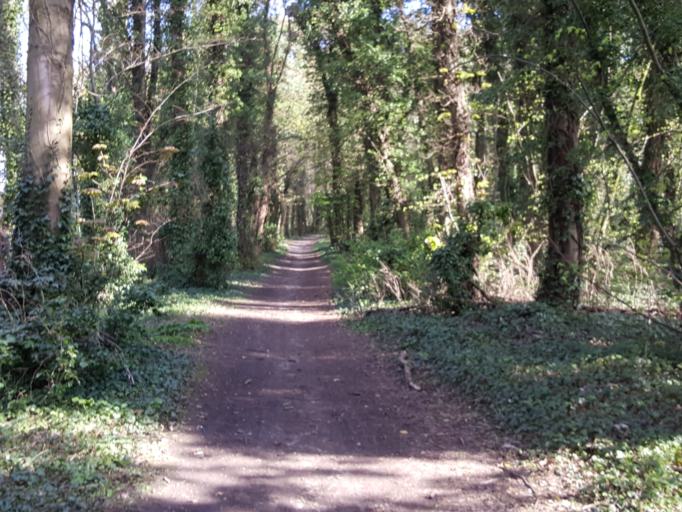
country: GB
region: England
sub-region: East Riding of Yorkshire
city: North Ferriby
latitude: 53.7253
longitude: -0.5175
